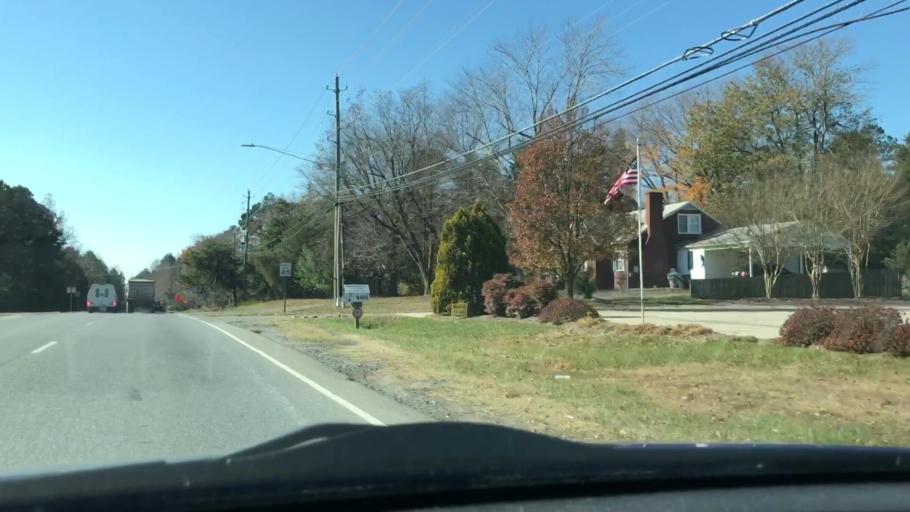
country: US
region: North Carolina
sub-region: Randolph County
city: Asheboro
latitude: 35.6826
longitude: -79.8447
